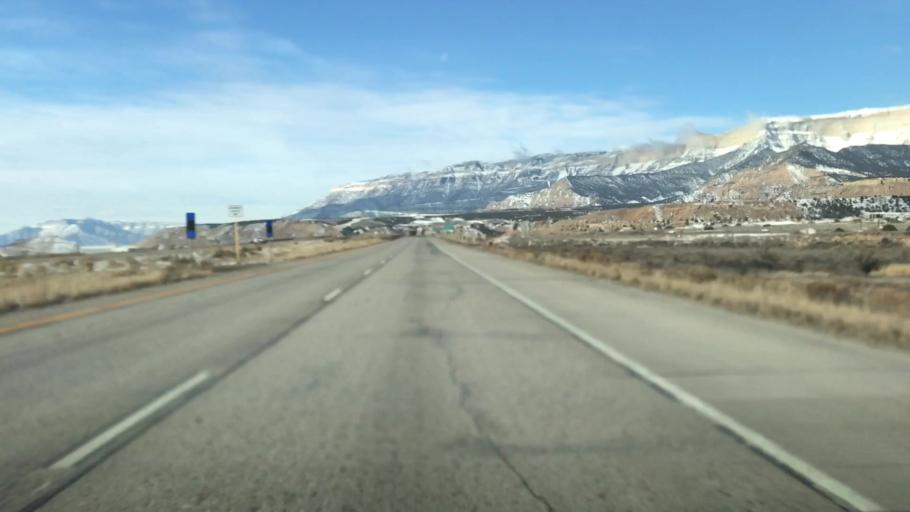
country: US
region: Colorado
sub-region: Garfield County
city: Rifle
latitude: 39.5205
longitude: -107.8338
